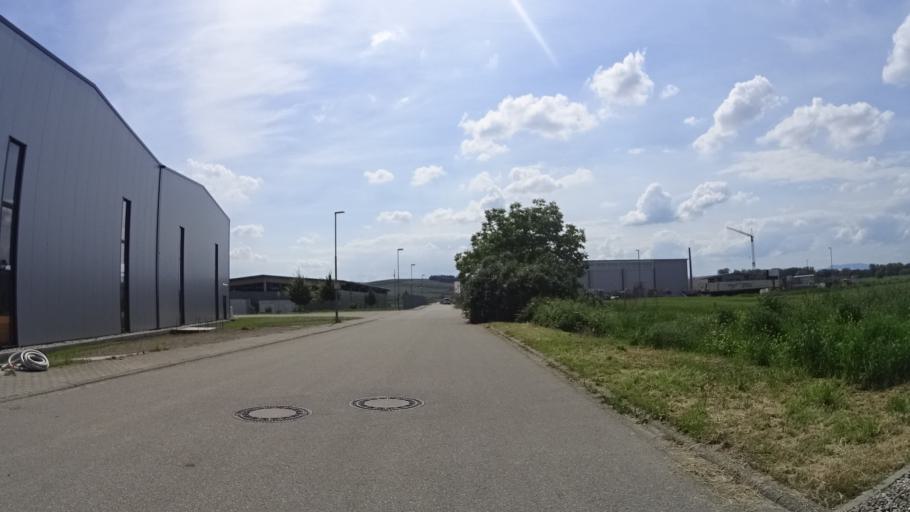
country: DE
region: Baden-Wuerttemberg
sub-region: Freiburg Region
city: Wyhl
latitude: 48.1620
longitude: 7.6338
